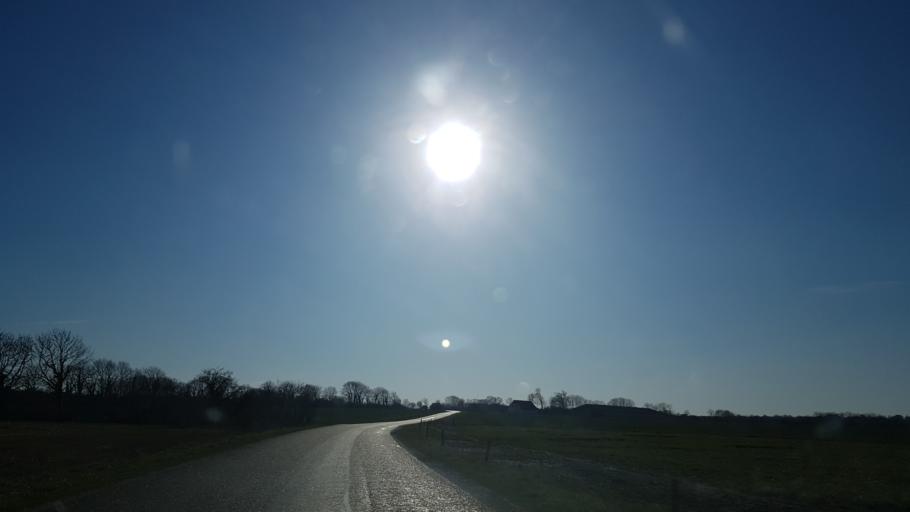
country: DK
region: South Denmark
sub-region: Vejen Kommune
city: Rodding
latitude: 55.3919
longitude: 9.0668
